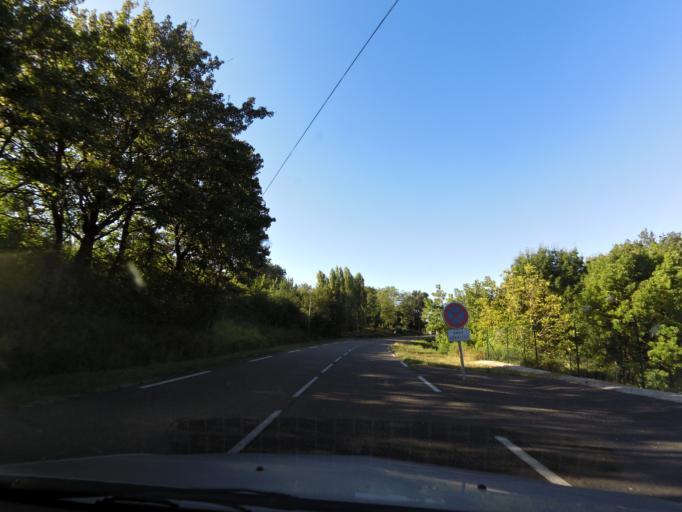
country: FR
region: Aquitaine
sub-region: Departement de la Gironde
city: Castets-en-Dorthe
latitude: 44.5010
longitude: -0.1493
